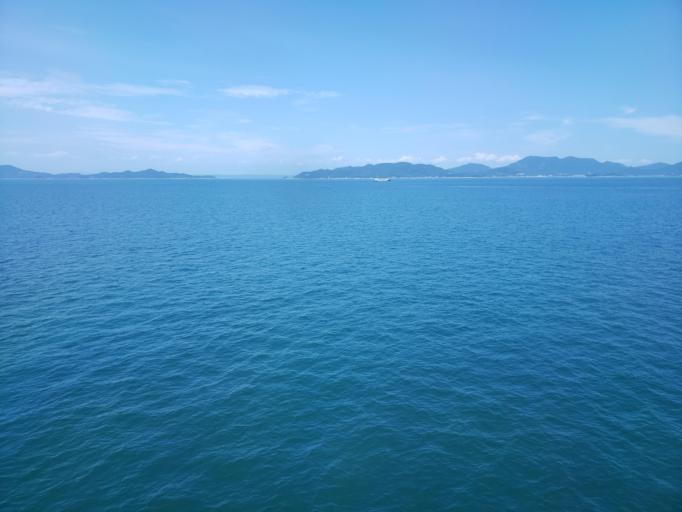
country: JP
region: Kagawa
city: Tonosho
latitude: 34.4057
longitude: 134.1520
